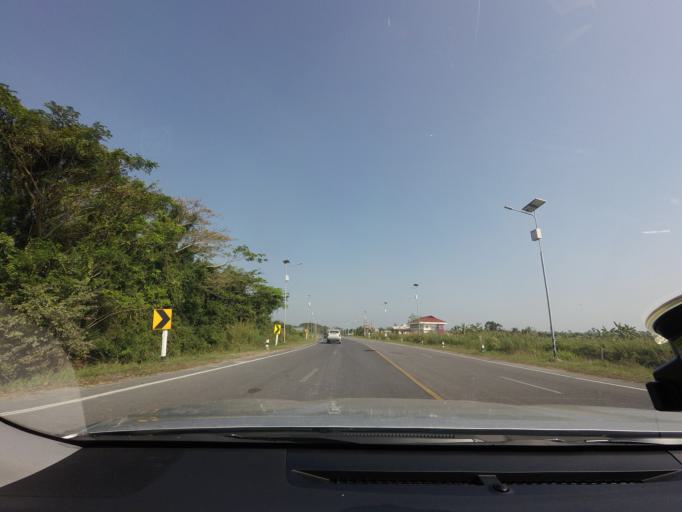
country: TH
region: Nakhon Si Thammarat
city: Nakhon Si Thammarat
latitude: 8.4914
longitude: 99.9742
